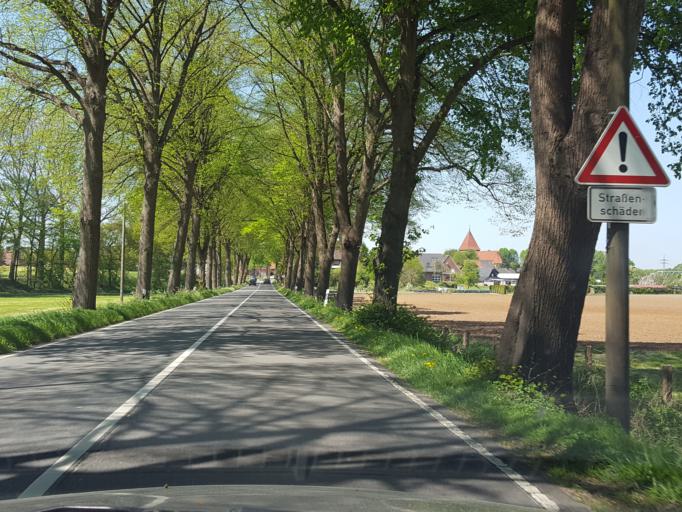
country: DE
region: North Rhine-Westphalia
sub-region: Regierungsbezirk Munster
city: Haltern
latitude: 51.7164
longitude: 7.2395
